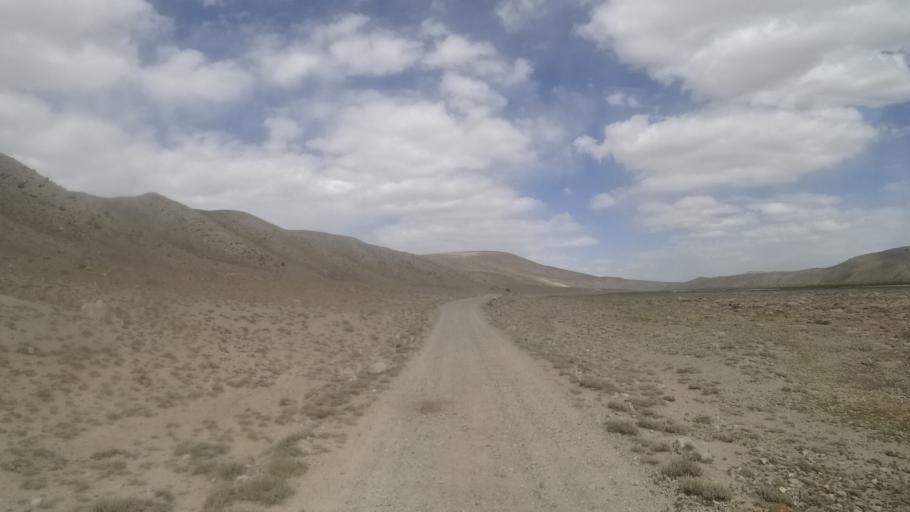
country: AF
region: Badakhshan
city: Khandud
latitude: 37.4070
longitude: 73.1507
